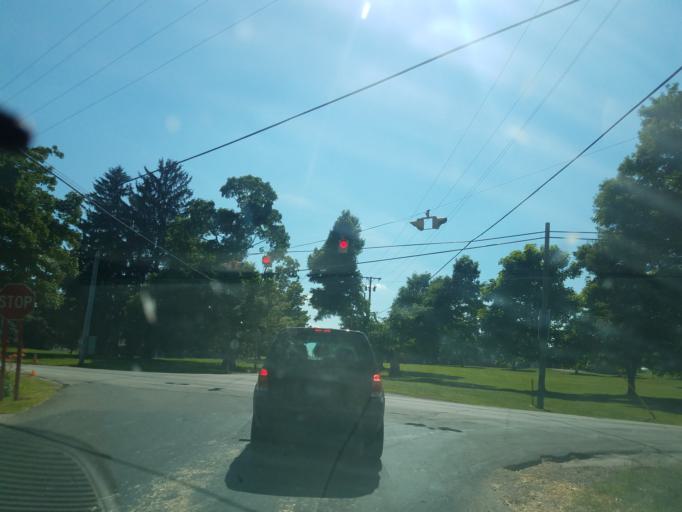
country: US
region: Ohio
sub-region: Portage County
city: Mantua
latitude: 41.2974
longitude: -81.2224
